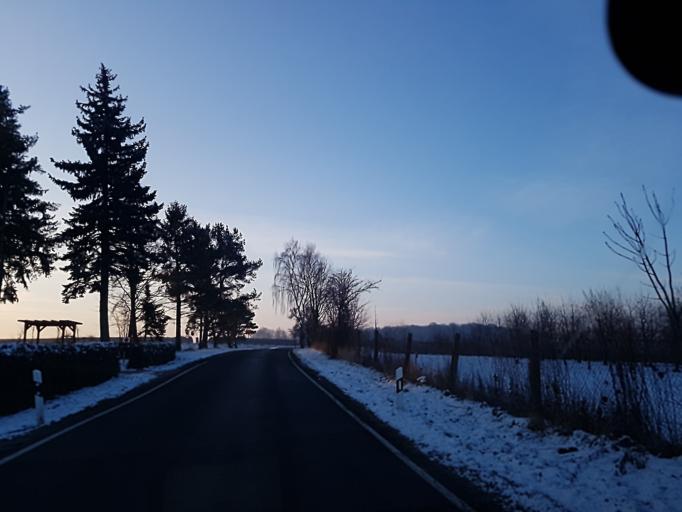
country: DE
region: Saxony
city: Mugeln
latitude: 51.2254
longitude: 13.0319
